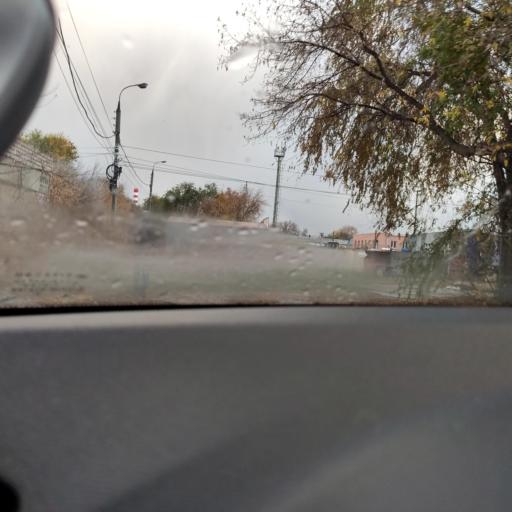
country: RU
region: Samara
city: Smyshlyayevka
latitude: 53.2057
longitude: 50.2843
